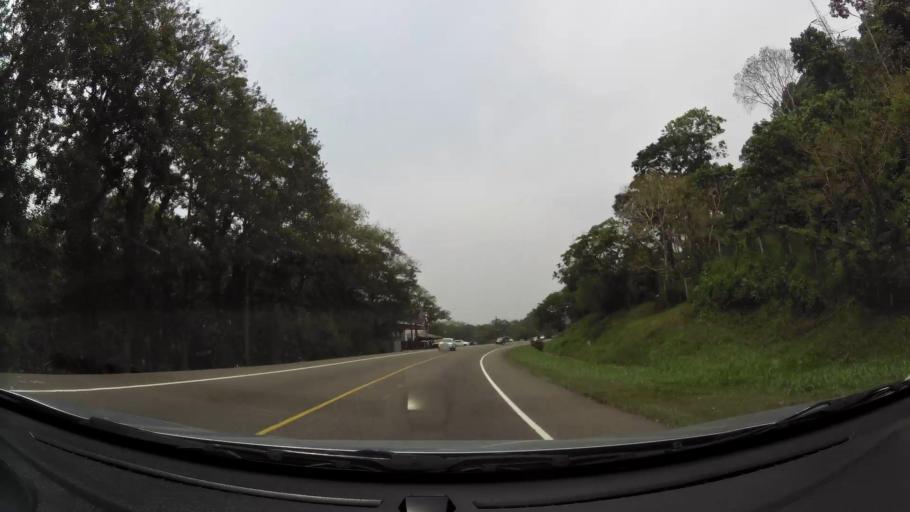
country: HN
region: Cortes
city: La Guama
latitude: 14.8716
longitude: -87.9482
